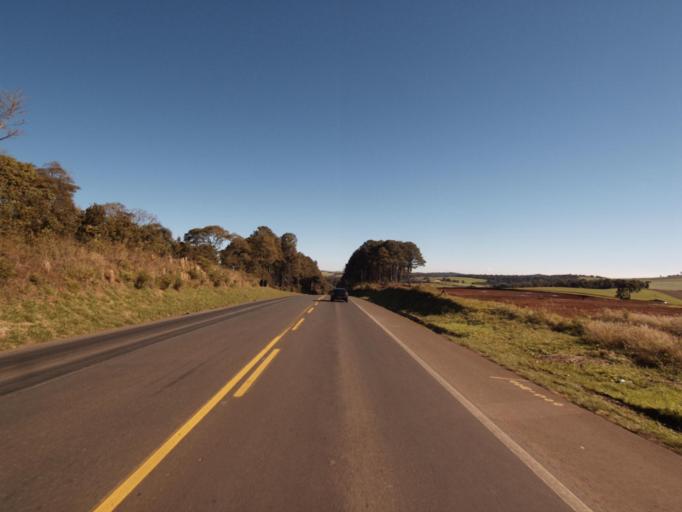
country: BR
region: Santa Catarina
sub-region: Xanxere
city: Xanxere
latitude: -26.9070
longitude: -52.4666
